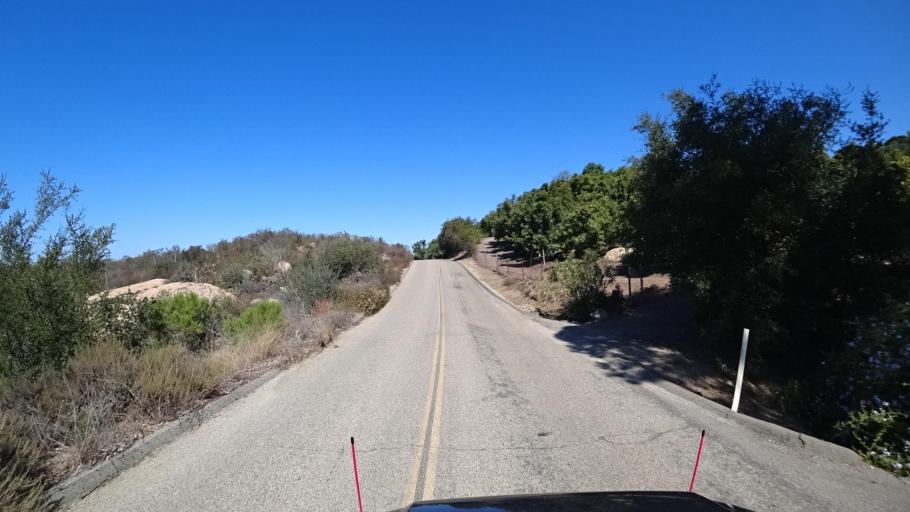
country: US
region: California
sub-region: San Diego County
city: Hidden Meadows
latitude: 33.2470
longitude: -117.0881
